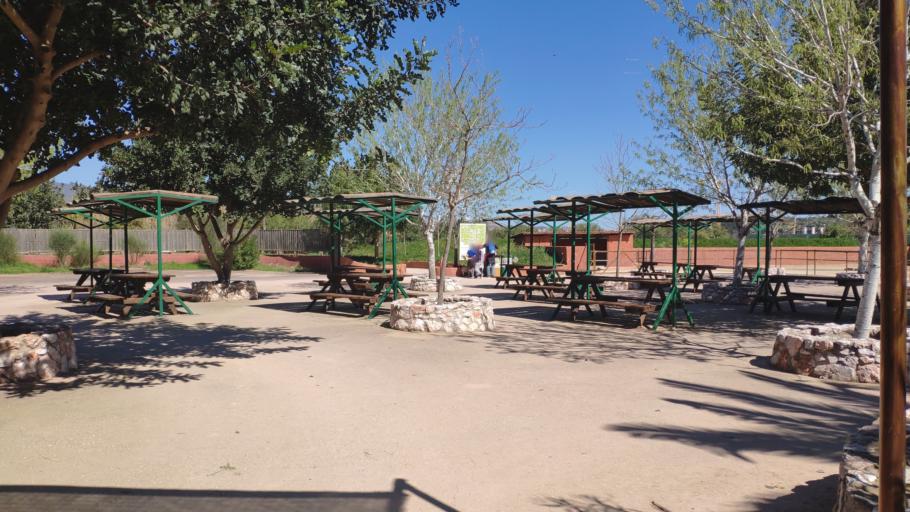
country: GR
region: Attica
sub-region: Nomarchia Anatolikis Attikis
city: Spata
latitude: 37.9809
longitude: 23.9109
